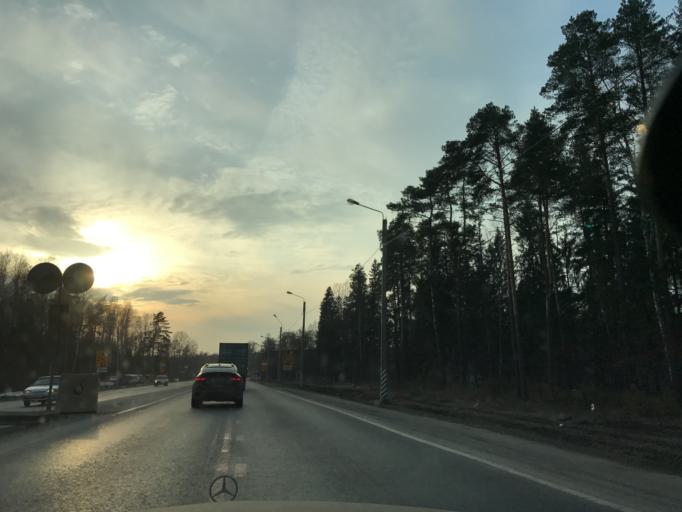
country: RU
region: Vladimir
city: Petushki
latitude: 55.9285
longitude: 39.3271
